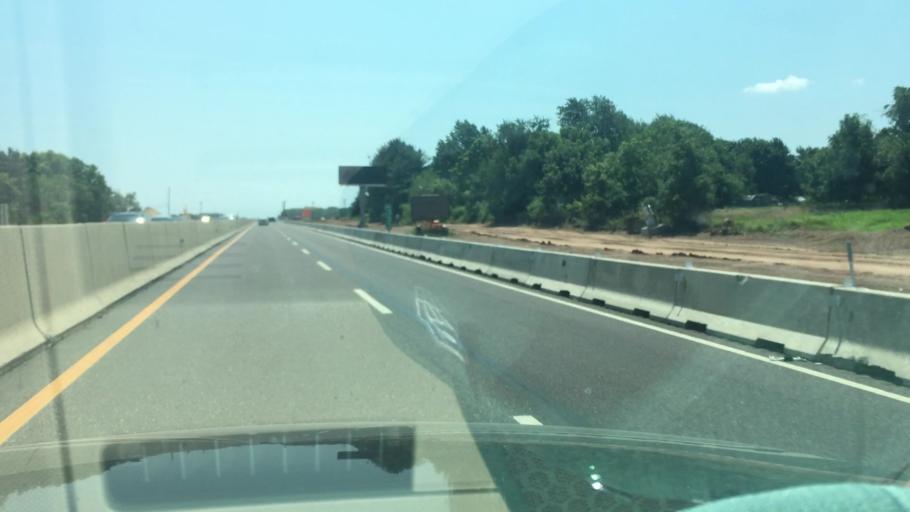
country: US
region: Pennsylvania
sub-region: Montgomery County
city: Harleysville
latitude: 40.2927
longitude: -75.3667
